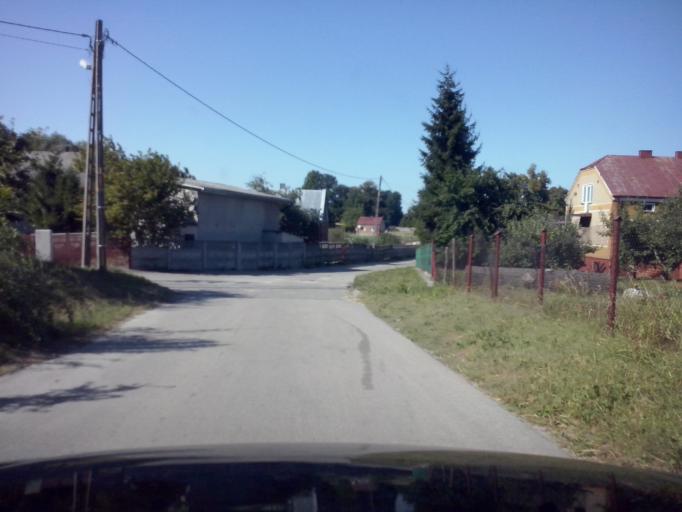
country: PL
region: Swietokrzyskie
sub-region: Powiat kielecki
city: Chmielnik
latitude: 50.6102
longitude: 20.7338
